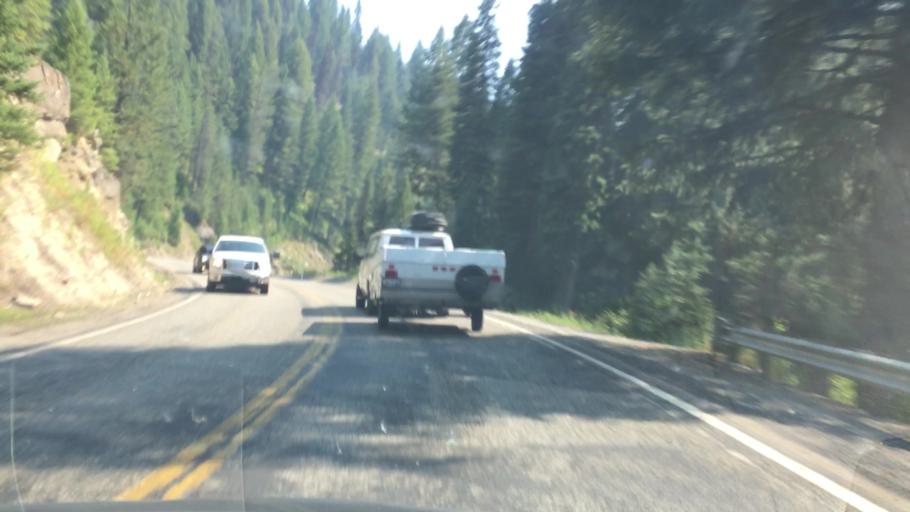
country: US
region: Idaho
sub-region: Valley County
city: Cascade
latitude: 44.3320
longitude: -116.0573
